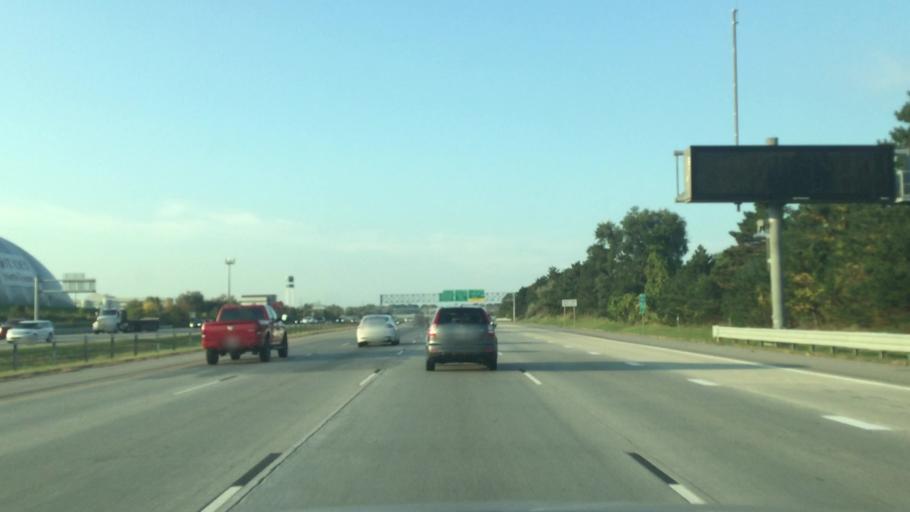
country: US
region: Michigan
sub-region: Wayne County
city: Northville
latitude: 42.4161
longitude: -83.4237
